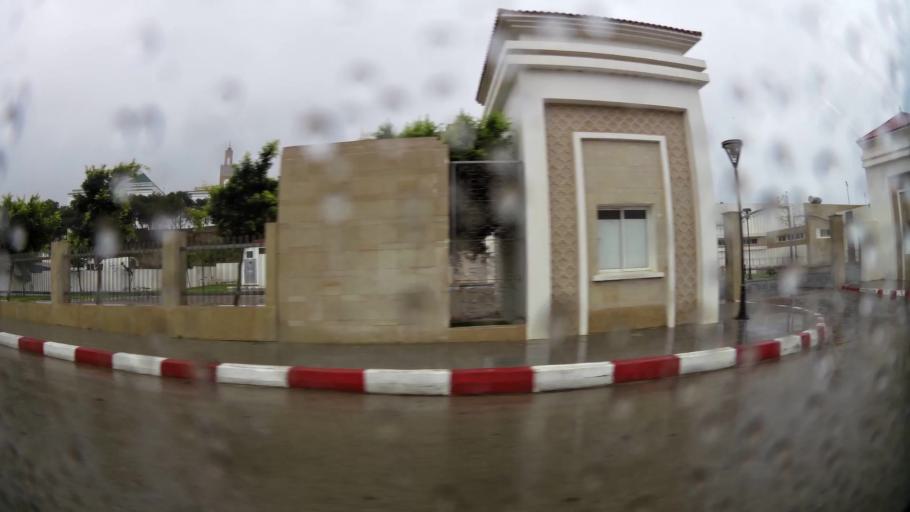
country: MA
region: Taza-Al Hoceima-Taounate
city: Al Hoceima
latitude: 35.2485
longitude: -3.9419
